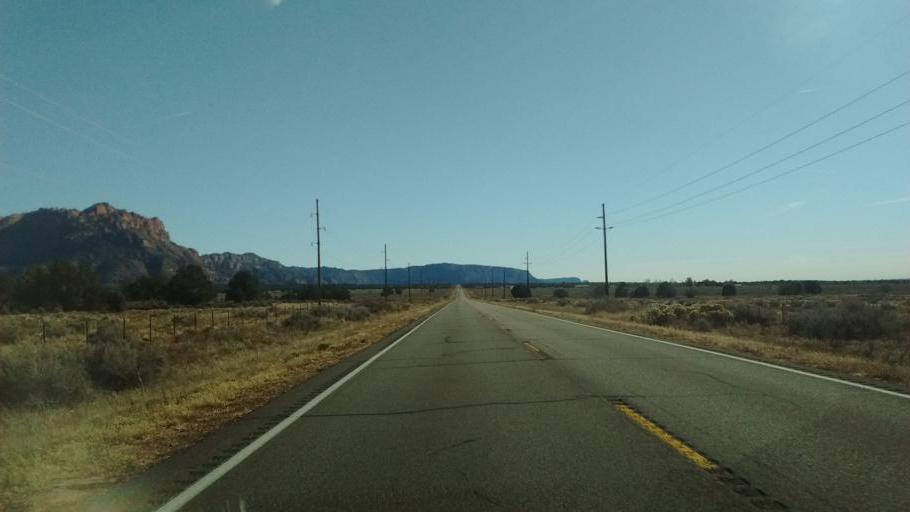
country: US
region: Arizona
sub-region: Mohave County
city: Colorado City
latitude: 37.0345
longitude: -113.0645
